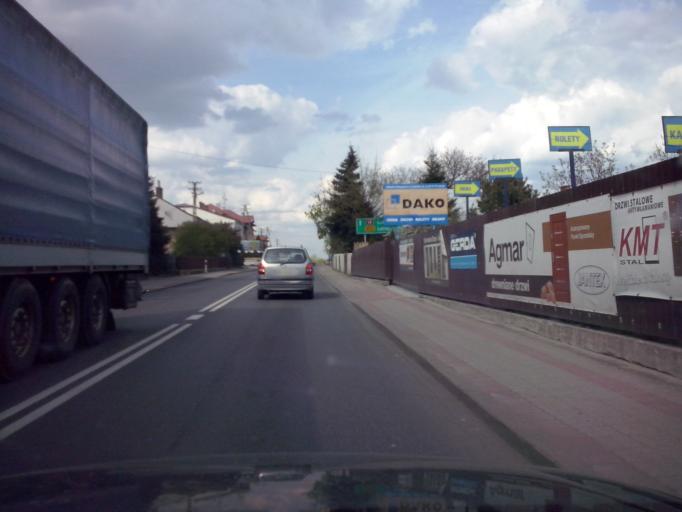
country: PL
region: Subcarpathian Voivodeship
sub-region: Powiat rzeszowski
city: Sokolow Malopolski
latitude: 50.2330
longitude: 22.1212
